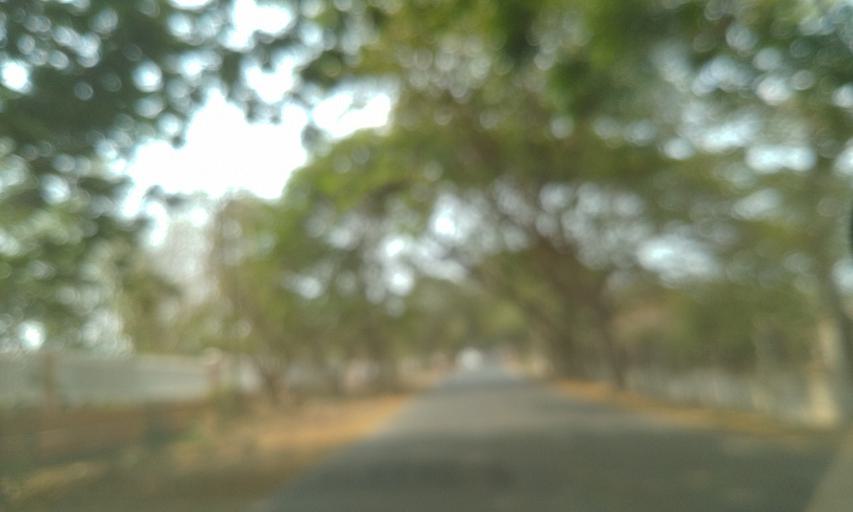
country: IN
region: Goa
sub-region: North Goa
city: Panaji
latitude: 15.4872
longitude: 73.8261
